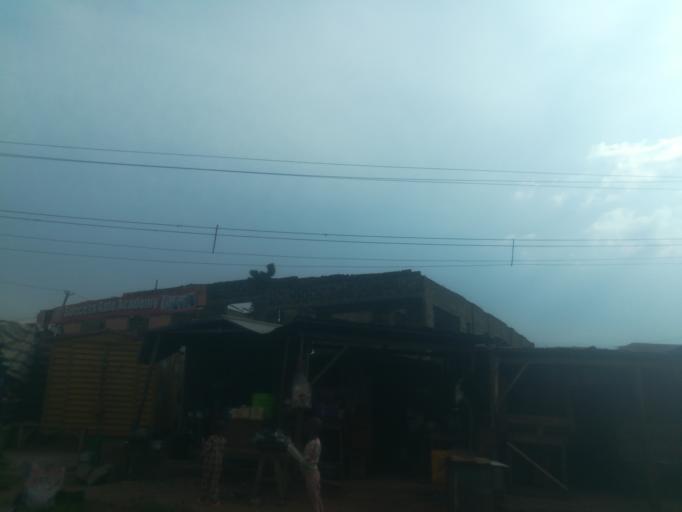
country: NG
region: Ogun
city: Abeokuta
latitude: 7.1364
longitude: 3.2972
